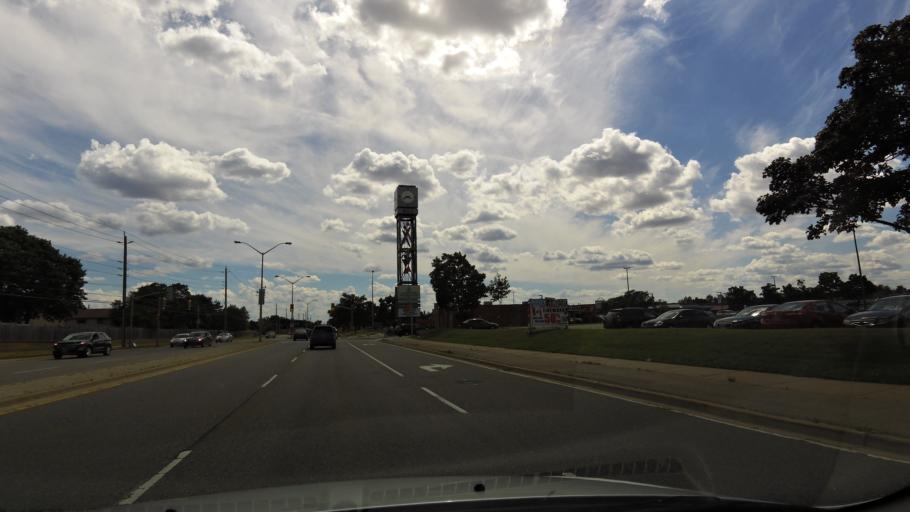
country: CA
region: Ontario
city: Oakville
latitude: 43.4829
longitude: -79.6932
